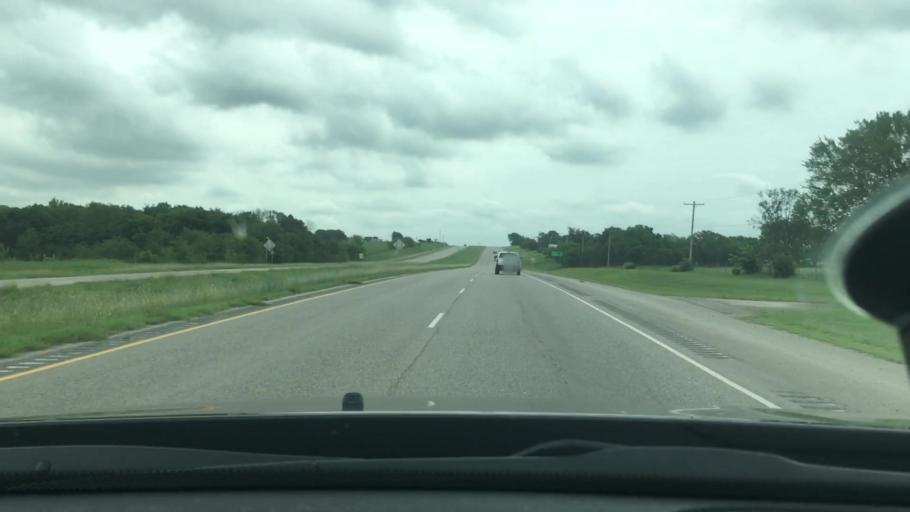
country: US
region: Oklahoma
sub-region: Carter County
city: Wilson
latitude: 34.1729
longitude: -97.4712
